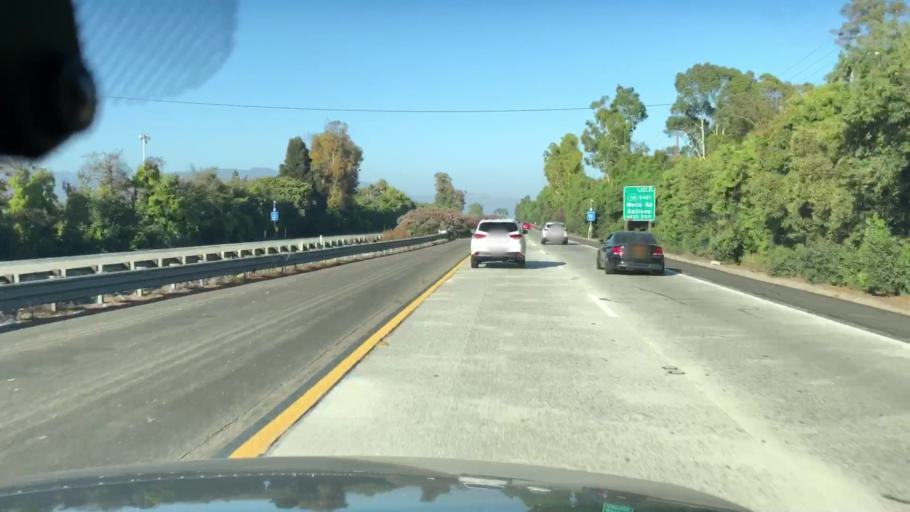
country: US
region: California
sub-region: Ventura County
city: Saticoy
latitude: 34.2799
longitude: -119.1725
